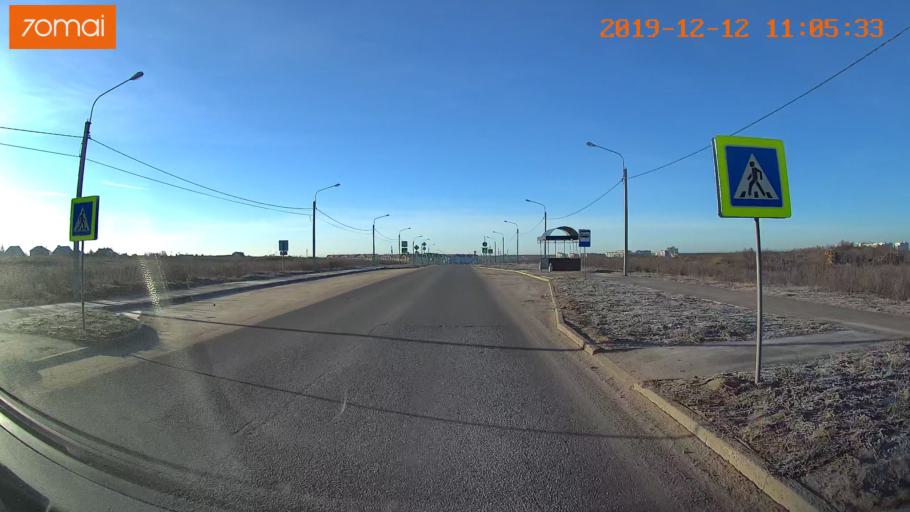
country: RU
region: Ivanovo
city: Kokhma
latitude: 56.9485
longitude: 41.0970
